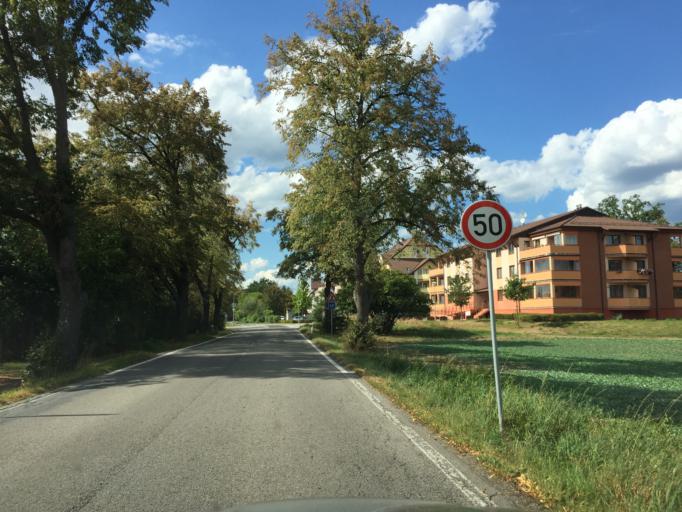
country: CZ
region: Jihocesky
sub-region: Okres Ceske Budejovice
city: Ceske Budejovice
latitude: 48.9540
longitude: 14.4799
